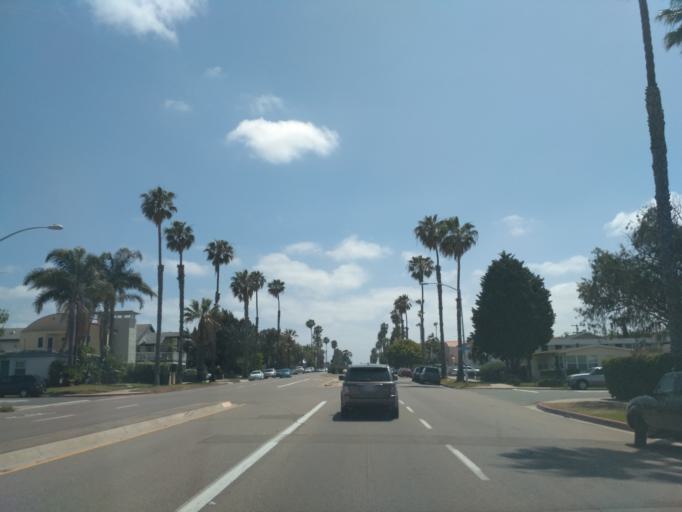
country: US
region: California
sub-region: San Diego County
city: La Jolla
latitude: 32.7969
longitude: -117.2445
